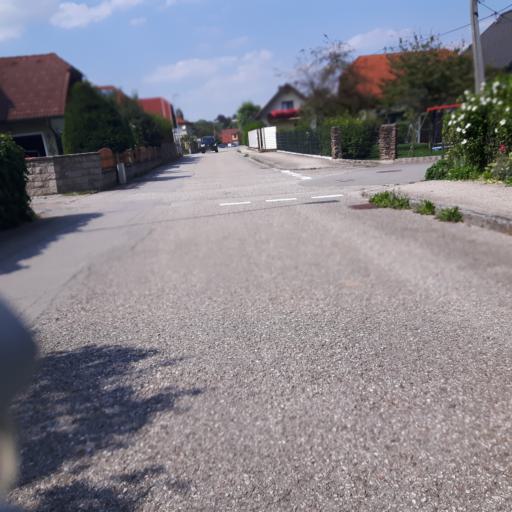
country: AT
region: Upper Austria
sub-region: Wels-Land
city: Stadl-Paura
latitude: 48.0830
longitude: 13.8673
